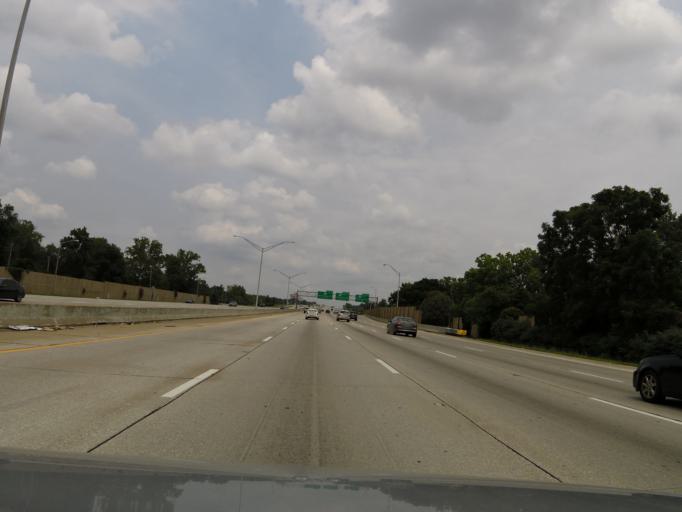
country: US
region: Kentucky
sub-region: Jefferson County
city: West Buechel
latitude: 38.2183
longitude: -85.6576
